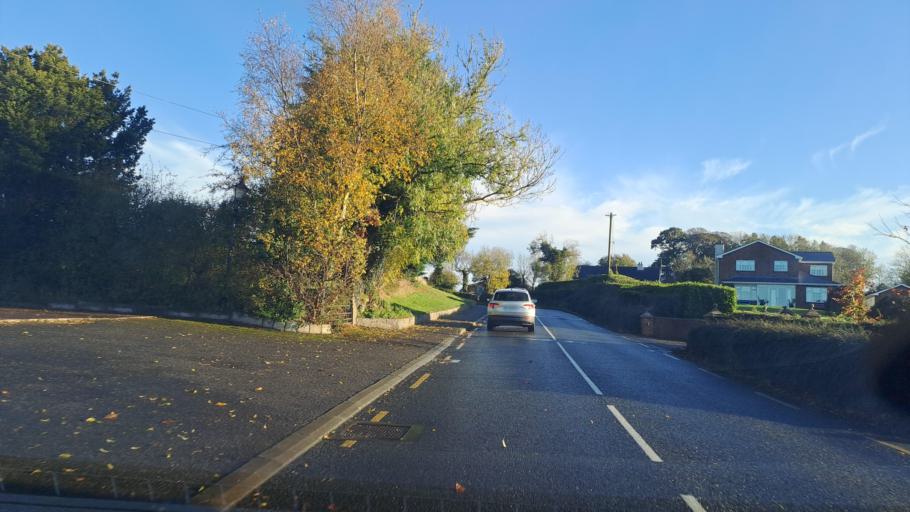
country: IE
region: Ulster
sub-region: An Cabhan
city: Cootehill
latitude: 54.1203
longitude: -7.0096
